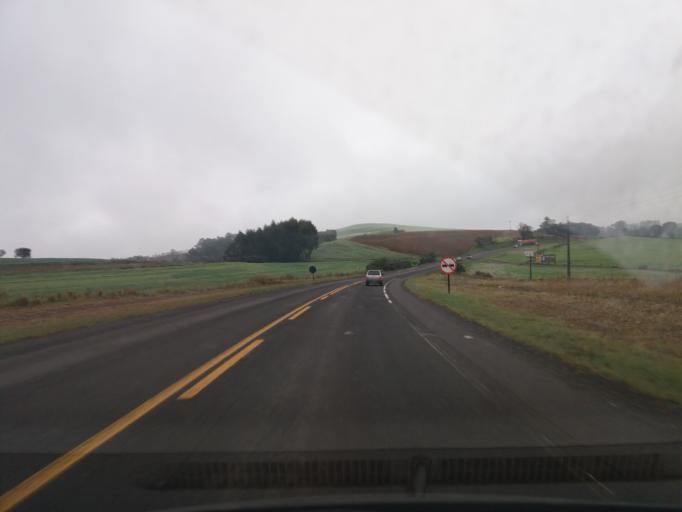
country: BR
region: Parana
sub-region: Realeza
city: Realeza
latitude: -25.8427
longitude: -53.5127
